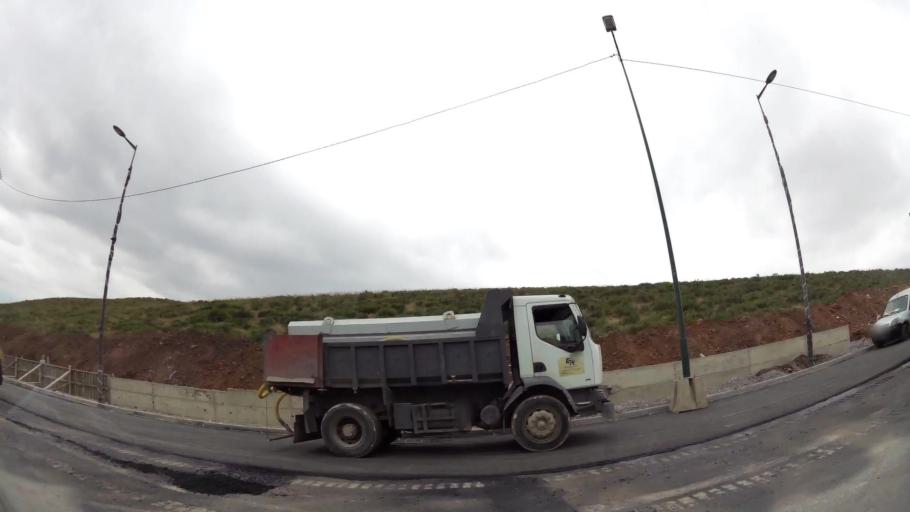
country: MA
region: Rabat-Sale-Zemmour-Zaer
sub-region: Rabat
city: Rabat
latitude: 33.9818
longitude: -6.8074
